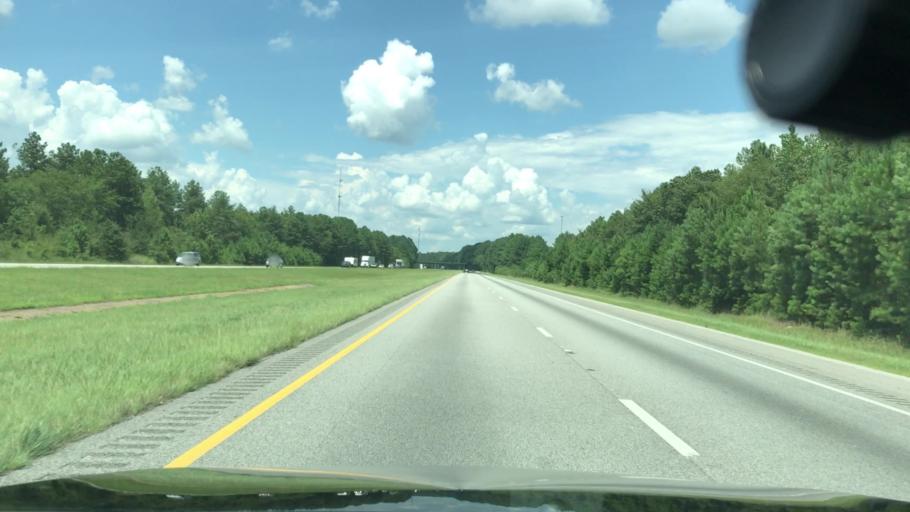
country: US
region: South Carolina
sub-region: Chester County
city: Great Falls
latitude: 34.5295
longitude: -80.9996
